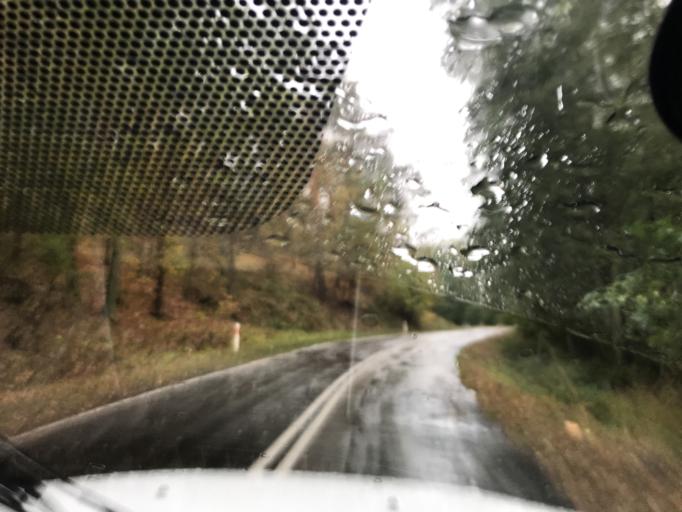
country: DE
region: Brandenburg
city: Neulewin
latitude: 52.7832
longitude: 14.2928
